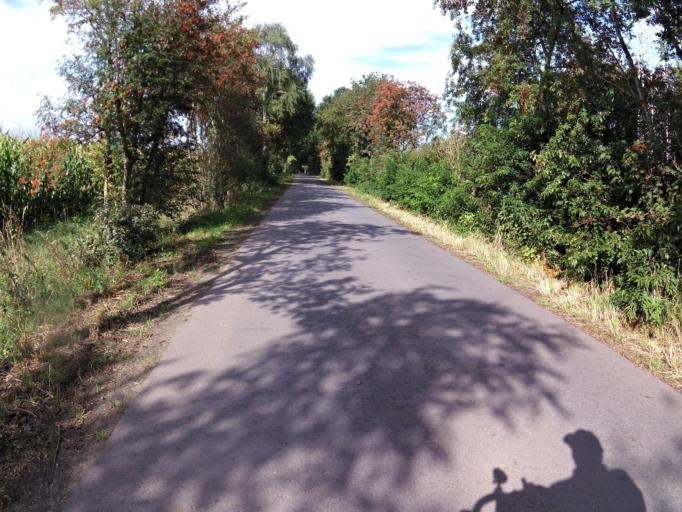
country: DE
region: Lower Saxony
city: Bremervorde
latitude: 53.4522
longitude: 9.1367
